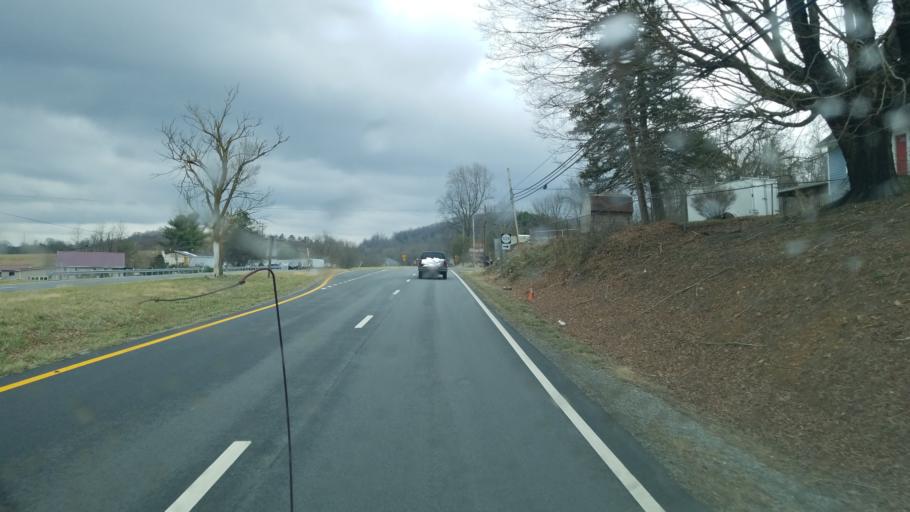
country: US
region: Virginia
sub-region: Giles County
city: Pearisburg
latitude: 37.3087
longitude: -80.7355
